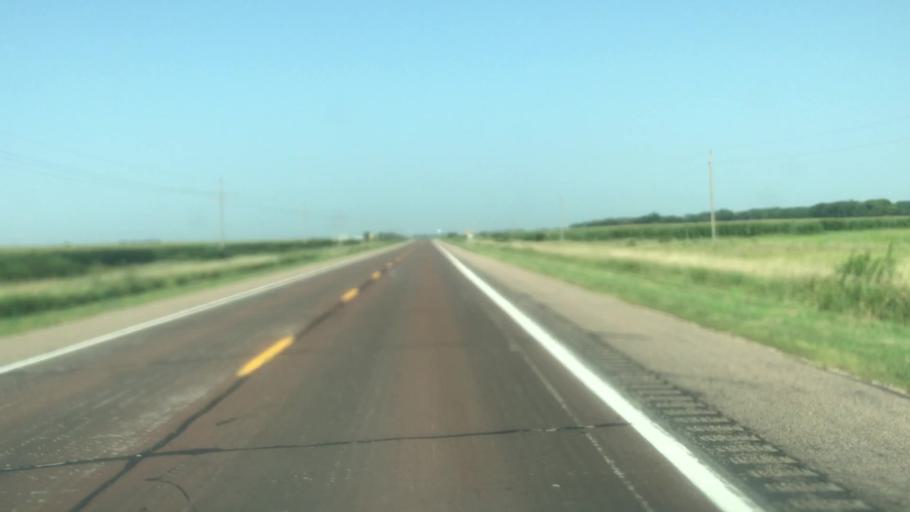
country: US
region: Nebraska
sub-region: Hall County
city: Grand Island
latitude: 40.9674
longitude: -98.4568
